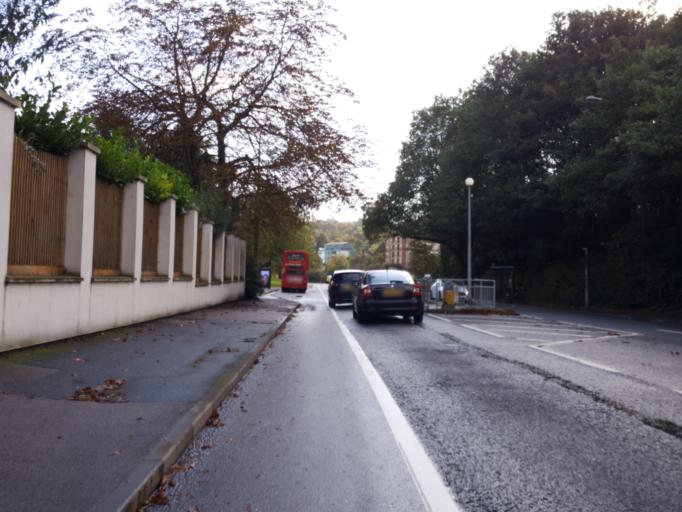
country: GB
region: England
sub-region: Brighton and Hove
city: Hove
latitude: 50.8562
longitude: -0.1540
